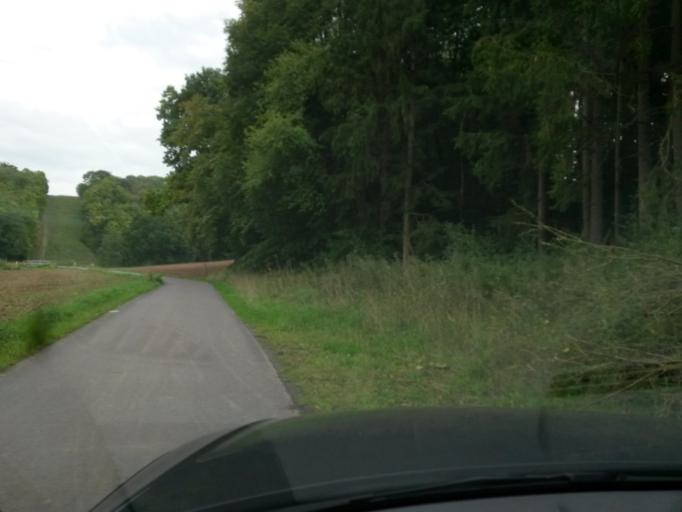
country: DE
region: Bavaria
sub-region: Regierungsbezirk Unterfranken
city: Gadheim
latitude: 49.8443
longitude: 9.9165
